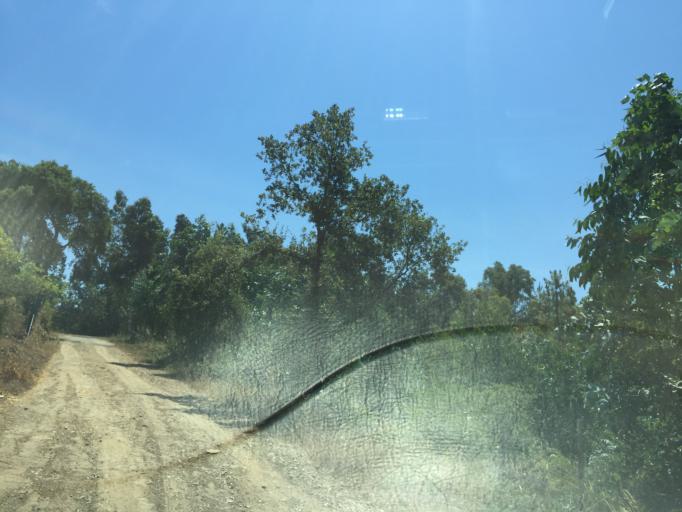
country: PT
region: Santarem
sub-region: Tomar
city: Tomar
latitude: 39.5970
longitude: -8.3544
